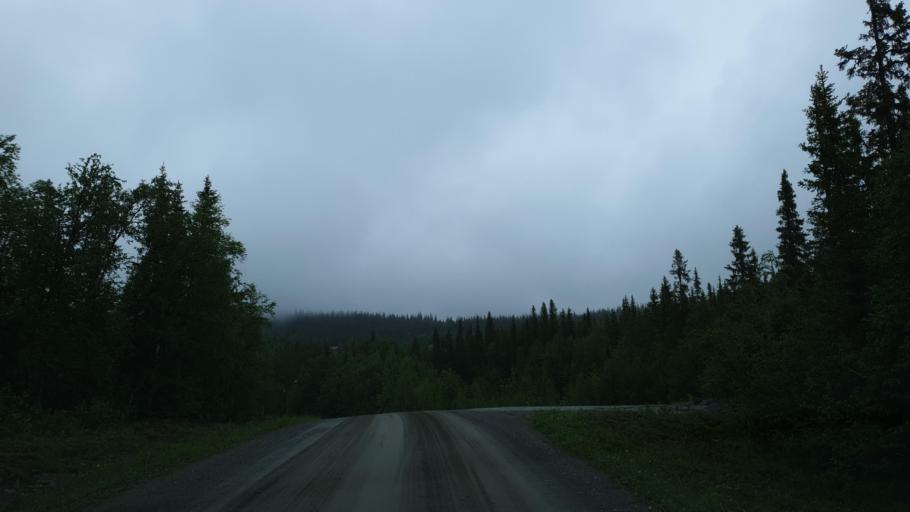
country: SE
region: Vaesterbotten
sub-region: Vilhelmina Kommun
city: Sjoberg
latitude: 65.3416
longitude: 15.8712
